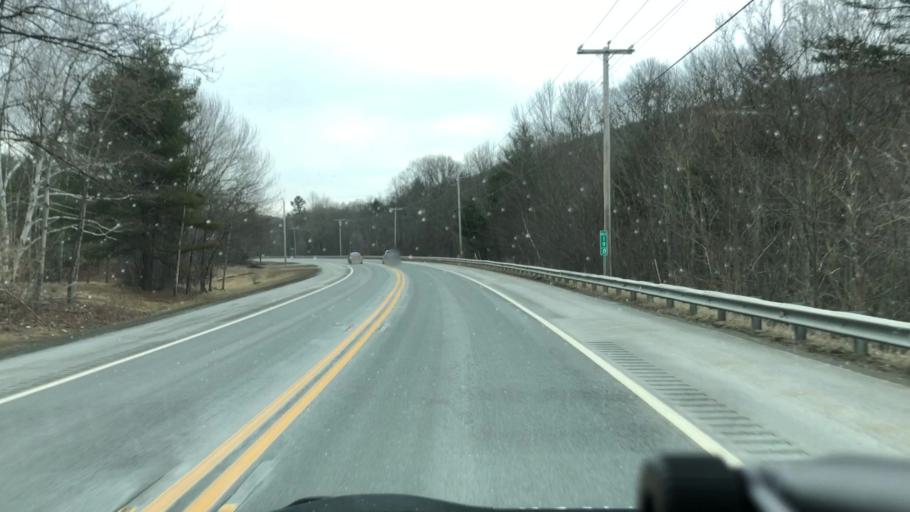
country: US
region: Massachusetts
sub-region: Hampshire County
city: Chesterfield
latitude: 42.4872
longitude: -72.9477
